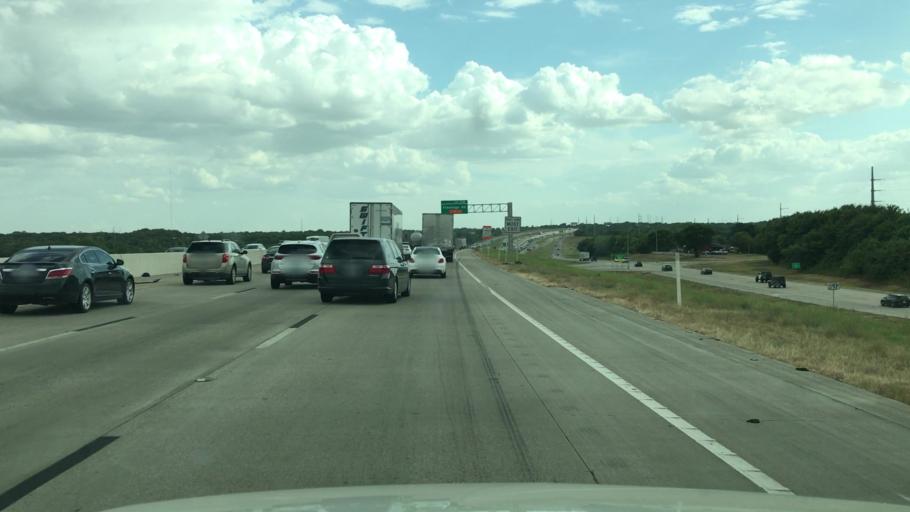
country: US
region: Texas
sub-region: McLennan County
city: Bruceville-Eddy
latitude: 31.3401
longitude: -97.2224
